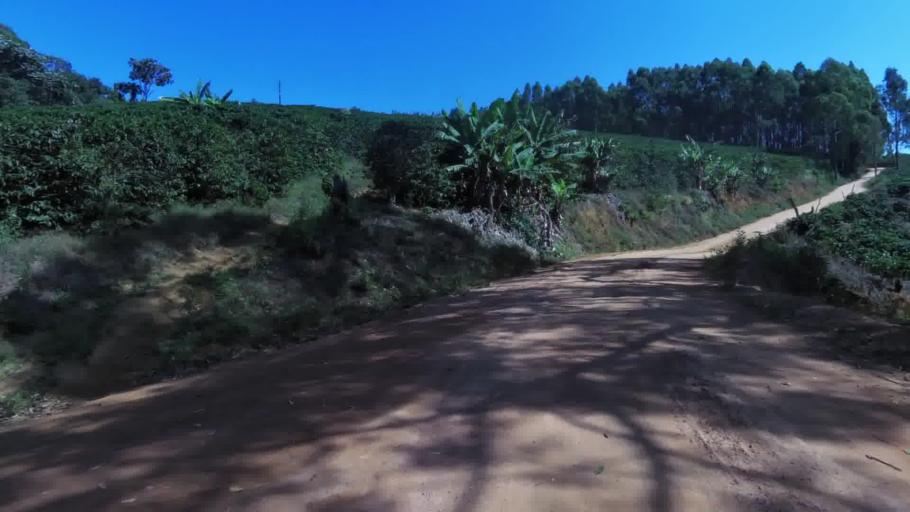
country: BR
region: Espirito Santo
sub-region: Alfredo Chaves
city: Alfredo Chaves
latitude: -20.5215
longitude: -40.8698
